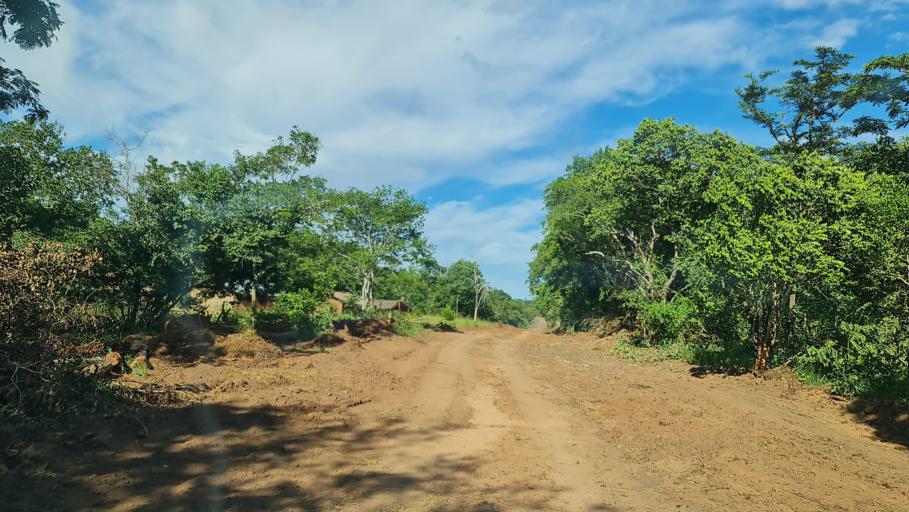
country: MZ
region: Nampula
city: Antonio Enes
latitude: -15.5088
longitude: 40.1376
